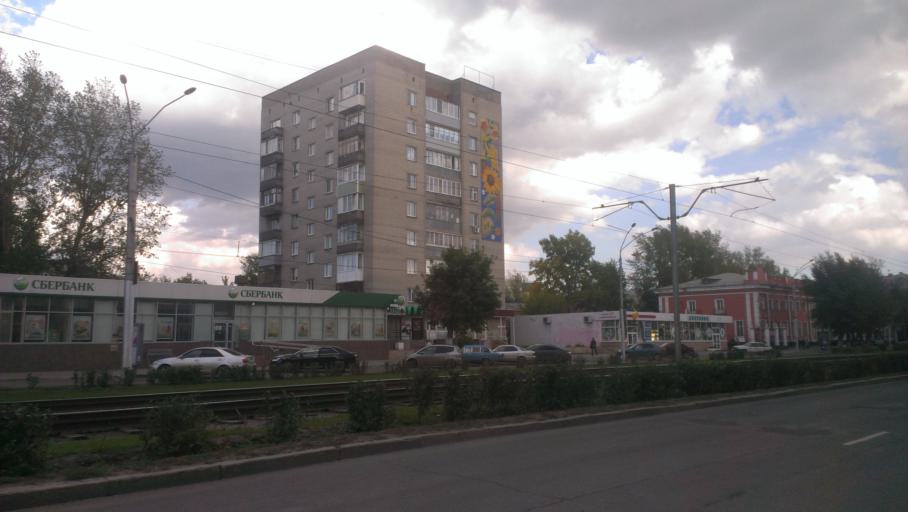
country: RU
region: Altai Krai
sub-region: Gorod Barnaulskiy
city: Barnaul
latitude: 53.3596
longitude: 83.7644
